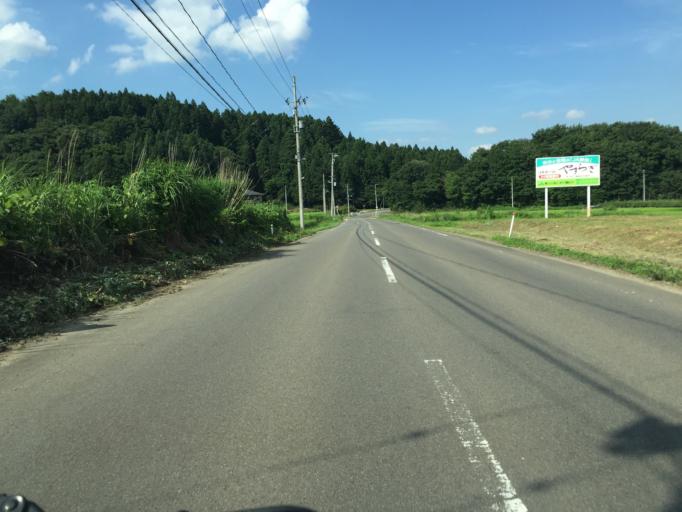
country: JP
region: Fukushima
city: Fukushima-shi
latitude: 37.7710
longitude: 140.3648
